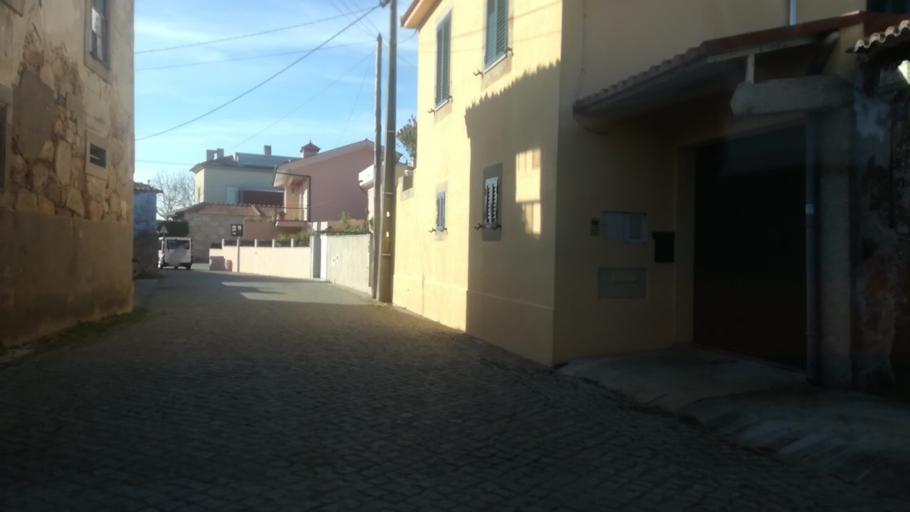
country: PT
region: Porto
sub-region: Matosinhos
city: Santa Cruz do Bispo
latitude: 41.2511
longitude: -8.6726
